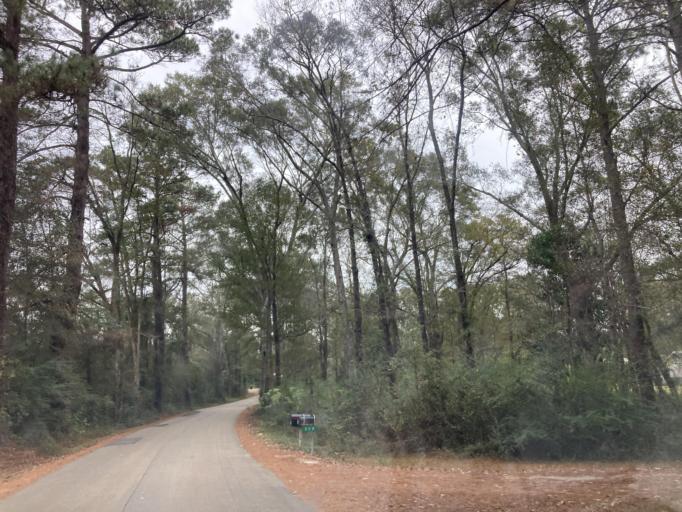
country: US
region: Mississippi
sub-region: Lamar County
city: Purvis
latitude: 31.1468
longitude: -89.4611
